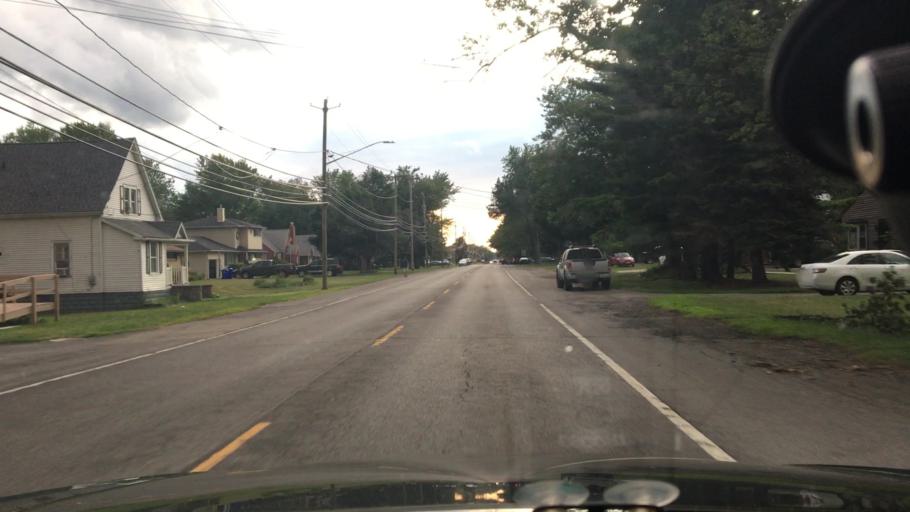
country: US
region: New York
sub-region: Erie County
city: West Seneca
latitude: 42.8396
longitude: -78.7568
